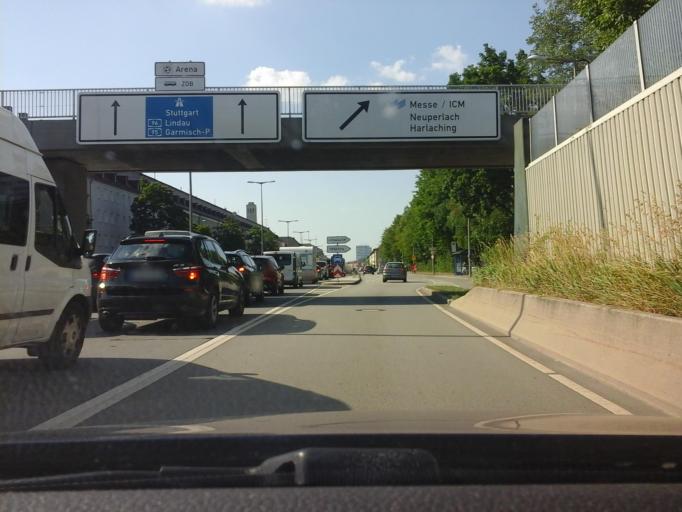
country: DE
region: Bavaria
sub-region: Upper Bavaria
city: Unterhaching
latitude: 48.0968
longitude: 11.5872
